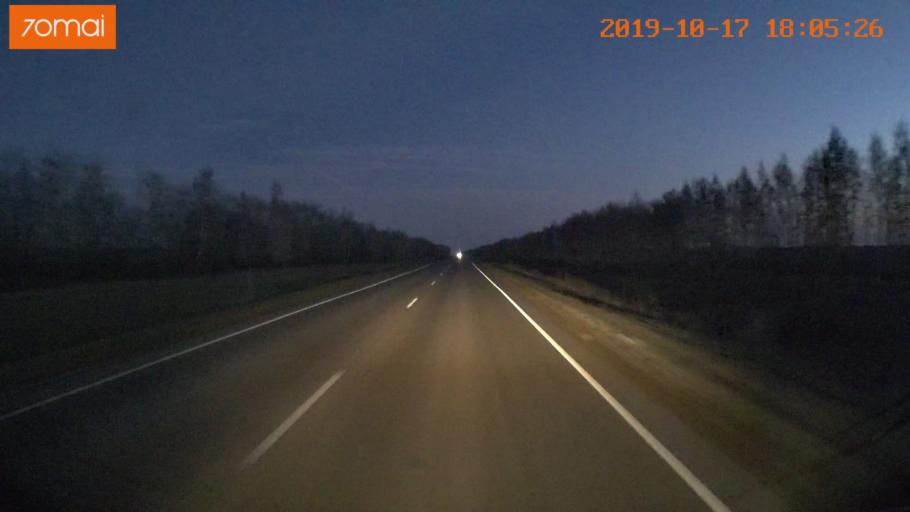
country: RU
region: Tula
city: Kurkino
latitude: 53.4665
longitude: 38.6439
